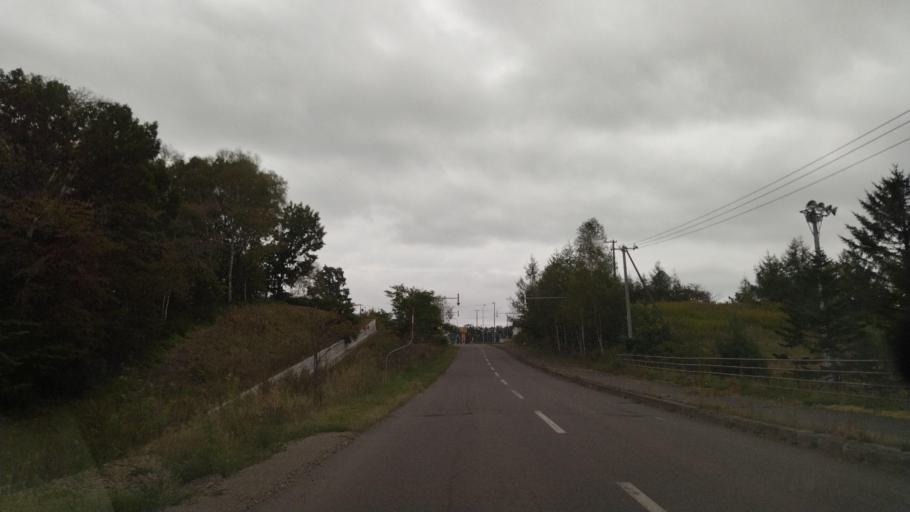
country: JP
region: Hokkaido
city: Otofuke
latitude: 43.2392
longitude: 143.3011
